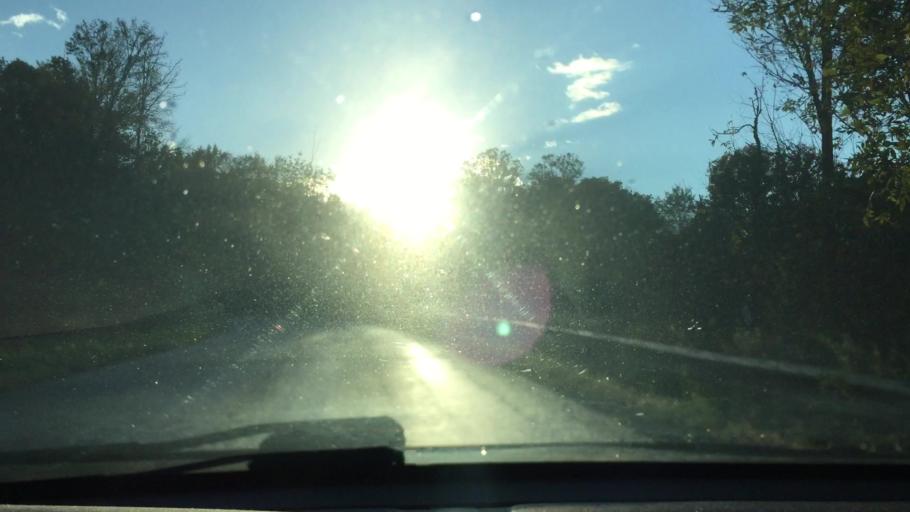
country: US
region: Pennsylvania
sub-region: Lawrence County
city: Bessemer
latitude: 41.0122
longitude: -80.4498
